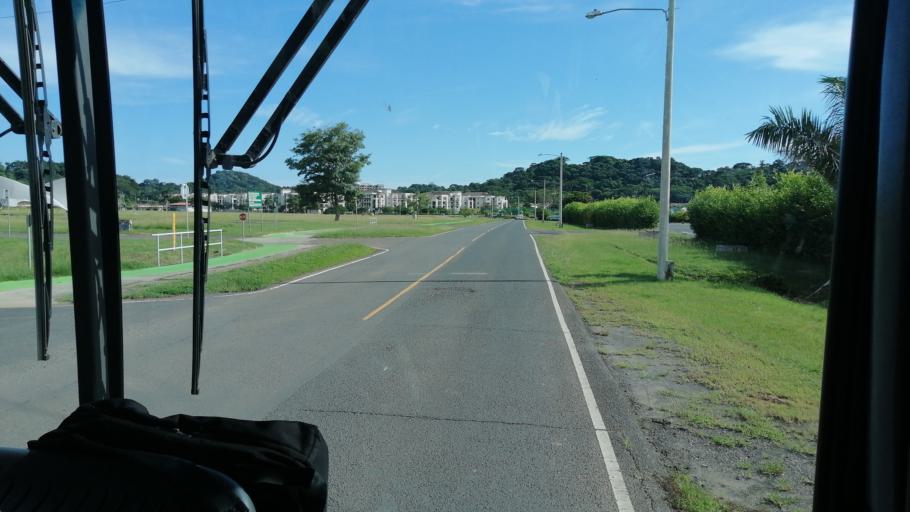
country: PA
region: Panama
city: Veracruz
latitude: 8.9107
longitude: -79.5920
